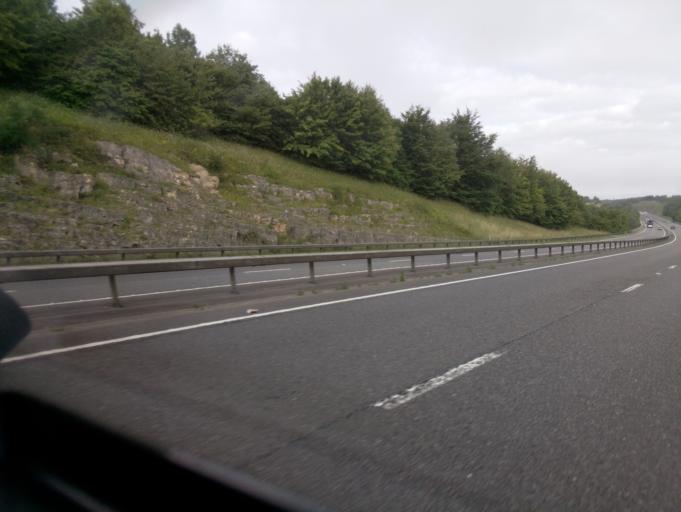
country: GB
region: England
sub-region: Gloucestershire
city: Cirencester
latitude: 51.7437
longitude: -1.9664
